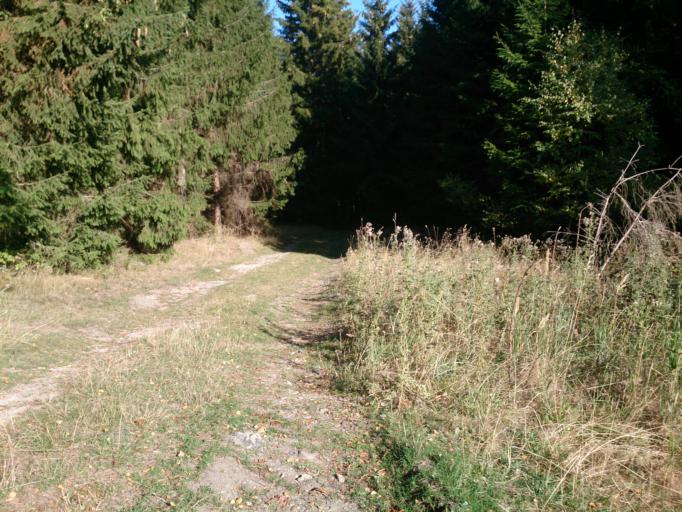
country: DE
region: Saxony-Anhalt
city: Darlingerode
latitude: 51.7830
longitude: 10.7277
